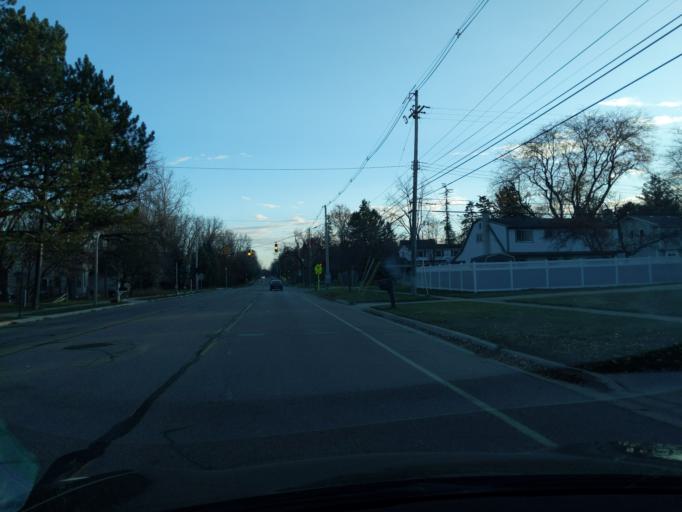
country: US
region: Michigan
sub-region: Ingham County
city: East Lansing
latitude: 42.7540
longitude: -84.4936
